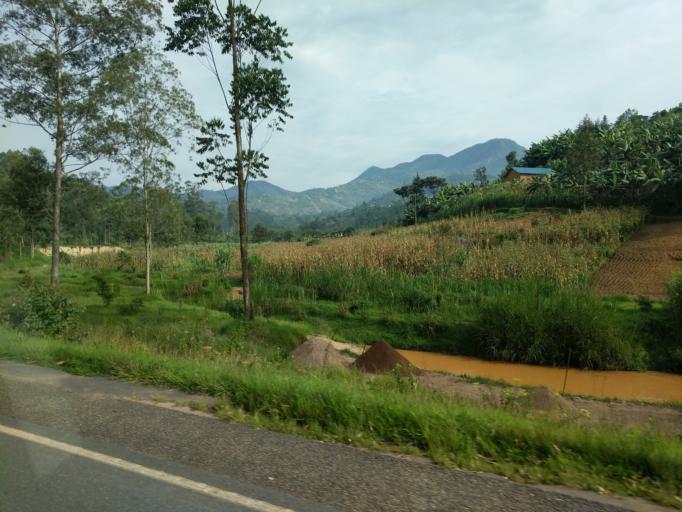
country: RW
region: Northern Province
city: Musanze
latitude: -1.6561
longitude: 29.8095
